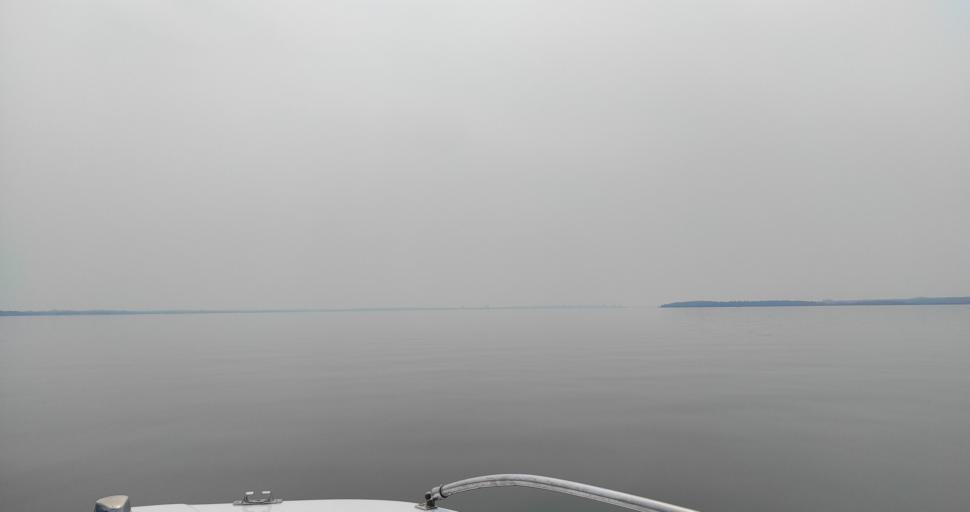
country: AR
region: Misiones
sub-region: Departamento de Candelaria
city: Candelaria
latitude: -27.4454
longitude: -55.7854
